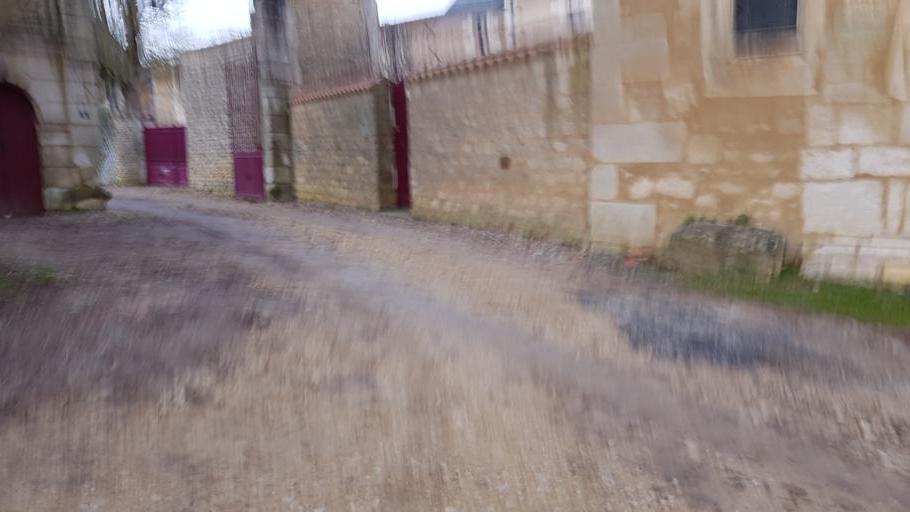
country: FR
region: Poitou-Charentes
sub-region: Departement de la Vienne
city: Avanton
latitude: 46.6648
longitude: 0.3085
